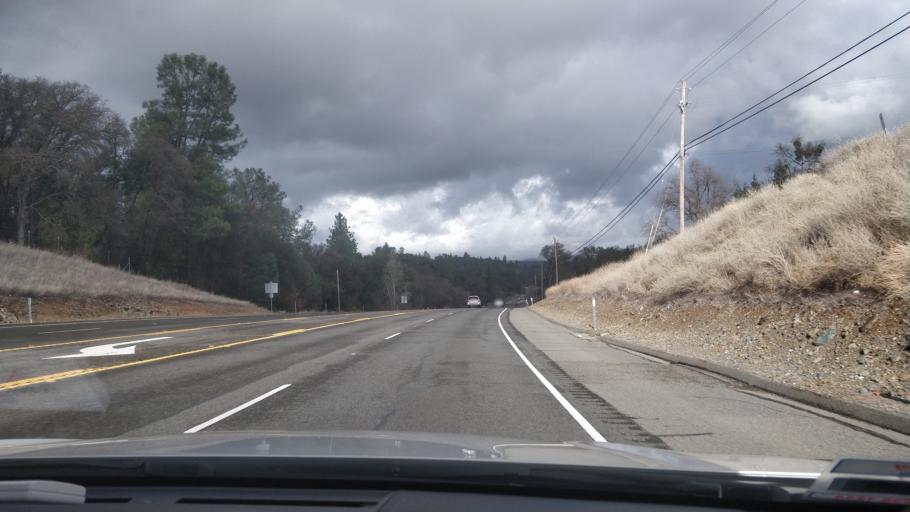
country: US
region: California
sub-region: Nevada County
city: Lake of the Pines
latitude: 39.0048
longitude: -121.1070
